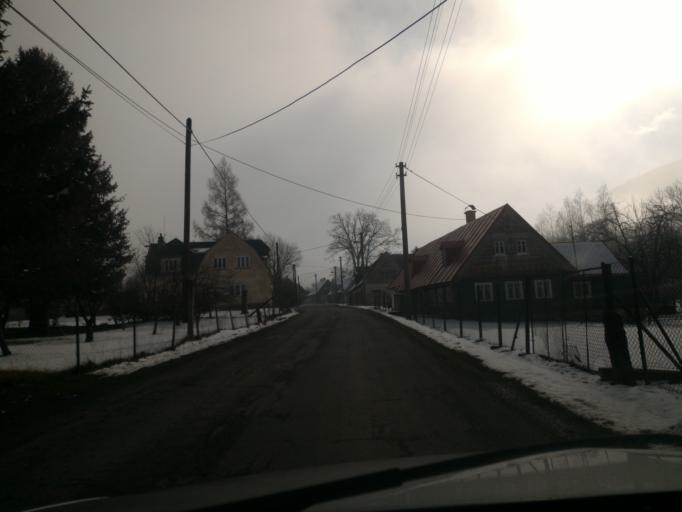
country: CZ
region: Liberecky
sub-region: Okres Liberec
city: Hejnice
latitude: 50.8733
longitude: 15.2233
